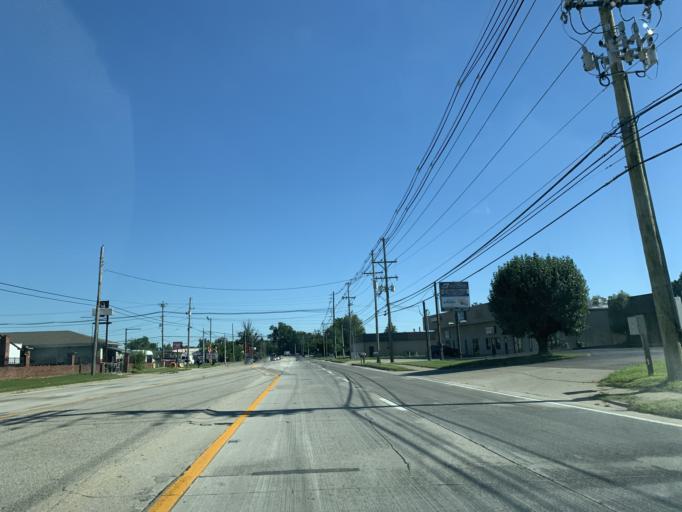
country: US
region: Kentucky
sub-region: Jefferson County
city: Audubon Park
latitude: 38.1859
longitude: -85.7008
